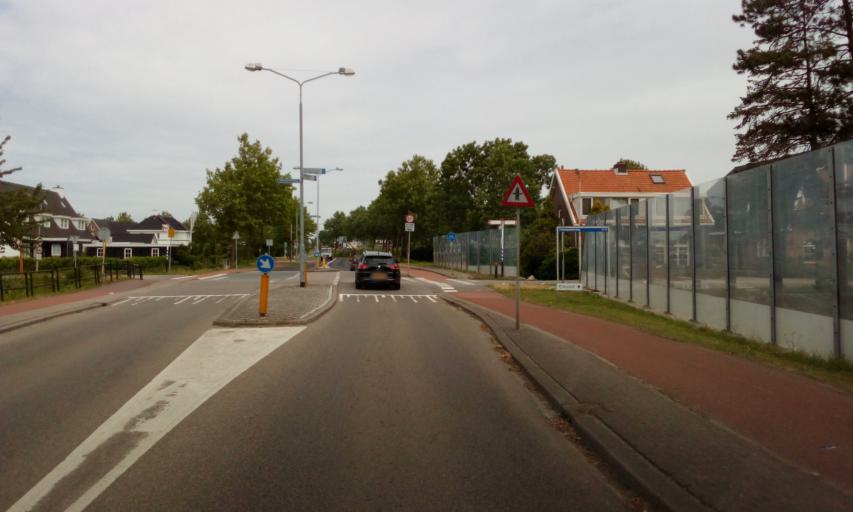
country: NL
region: South Holland
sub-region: Gemeente Alblasserdam
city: Alblasserdam
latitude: 51.8599
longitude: 4.6751
